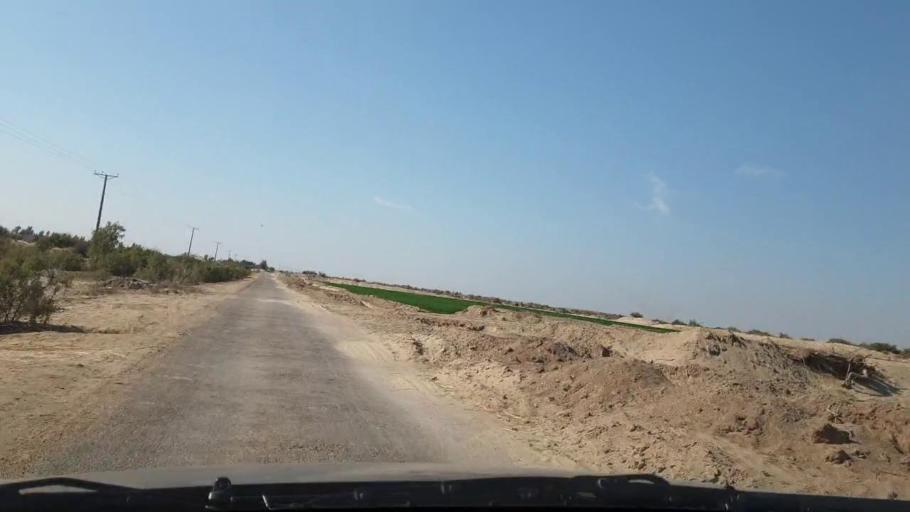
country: PK
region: Sindh
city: Khadro
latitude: 26.2696
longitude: 68.7910
